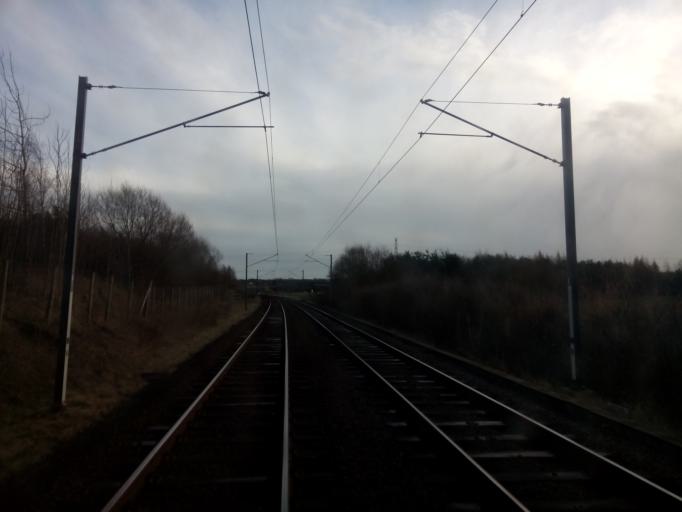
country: GB
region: England
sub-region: Newcastle upon Tyne
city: Dinnington
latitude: 55.0199
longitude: -1.6939
